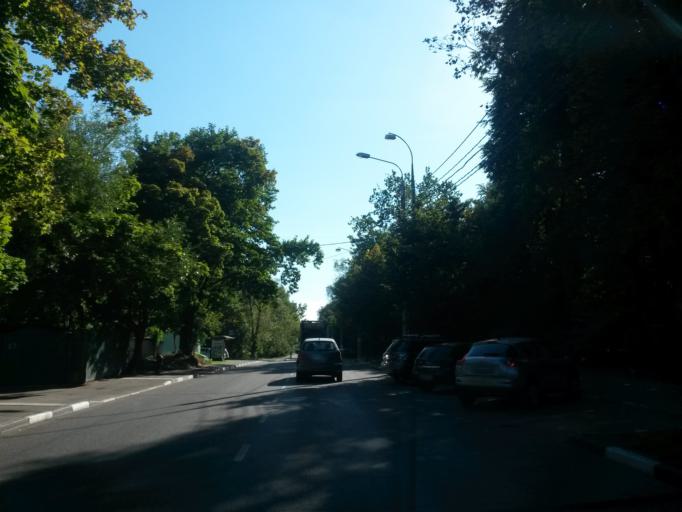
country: RU
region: Moscow
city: Zyuzino
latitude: 55.6579
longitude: 37.5857
